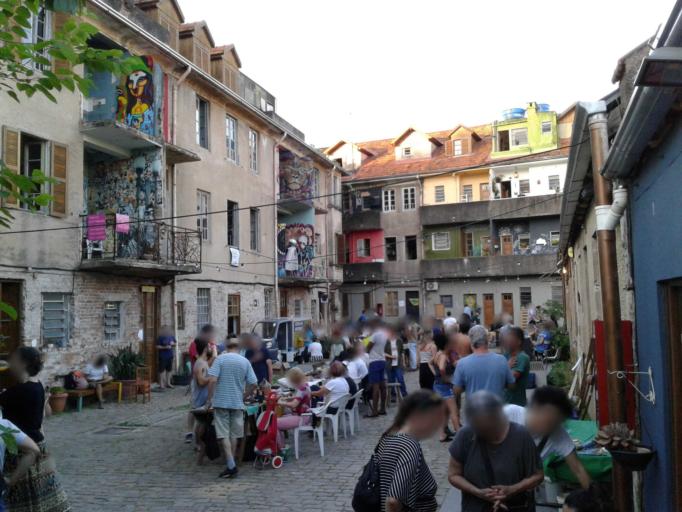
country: BR
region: Rio Grande do Sul
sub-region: Porto Alegre
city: Porto Alegre
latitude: -30.0201
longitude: -51.2094
